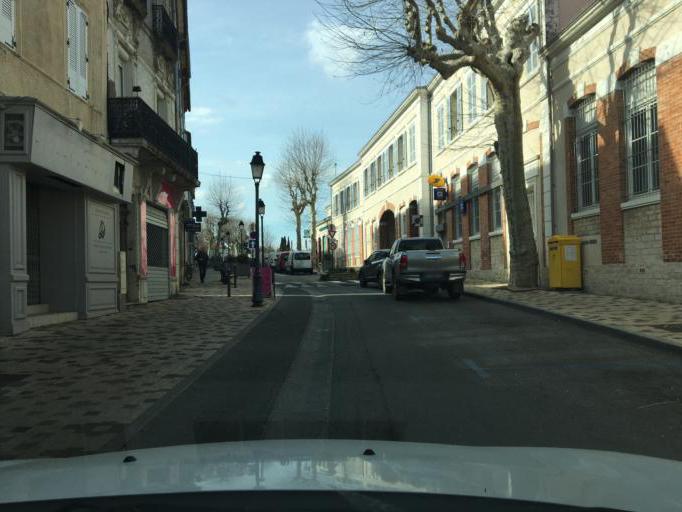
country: FR
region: Provence-Alpes-Cote d'Azur
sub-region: Departement du Var
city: Flayosc
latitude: 43.5344
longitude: 6.3954
